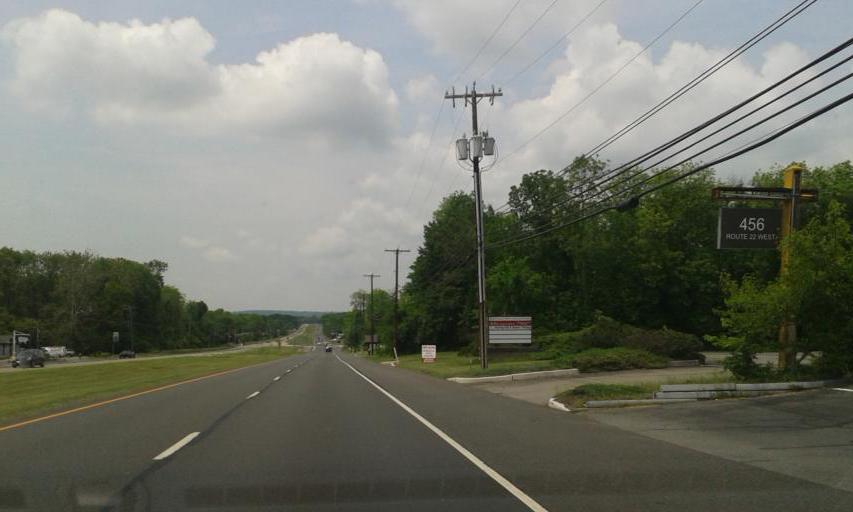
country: US
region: New Jersey
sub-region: Hunterdon County
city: Whitehouse Station
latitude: 40.6296
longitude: -74.7771
